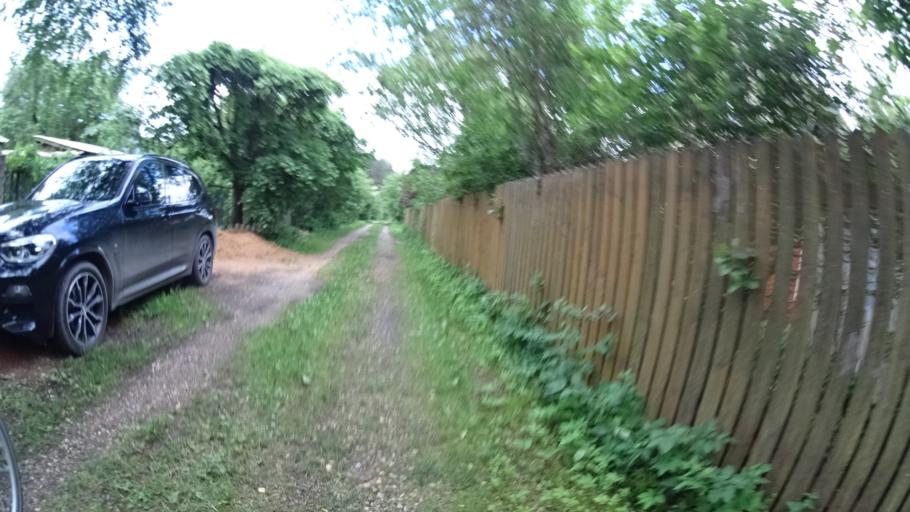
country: RU
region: Moskovskaya
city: Zelenogradskiy
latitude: 56.1237
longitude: 37.9059
